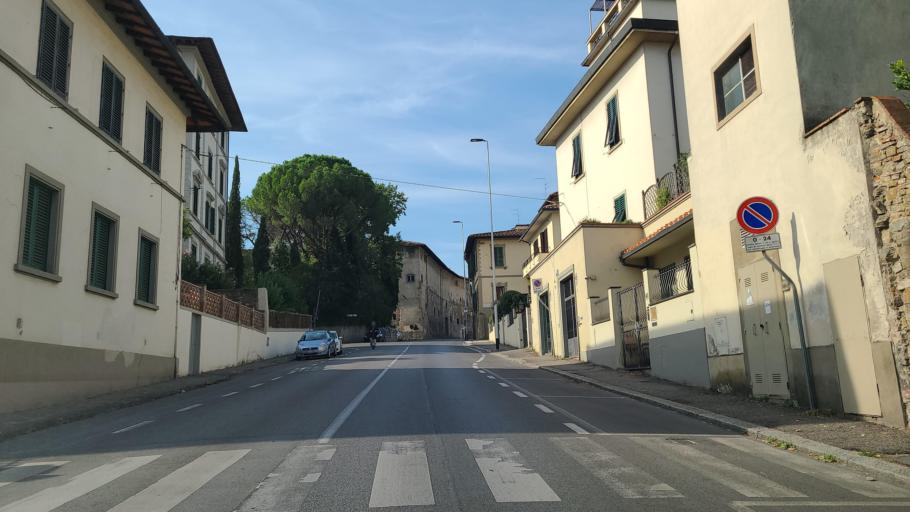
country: IT
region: Tuscany
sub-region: Province of Florence
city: Florence
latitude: 43.7537
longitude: 11.2393
